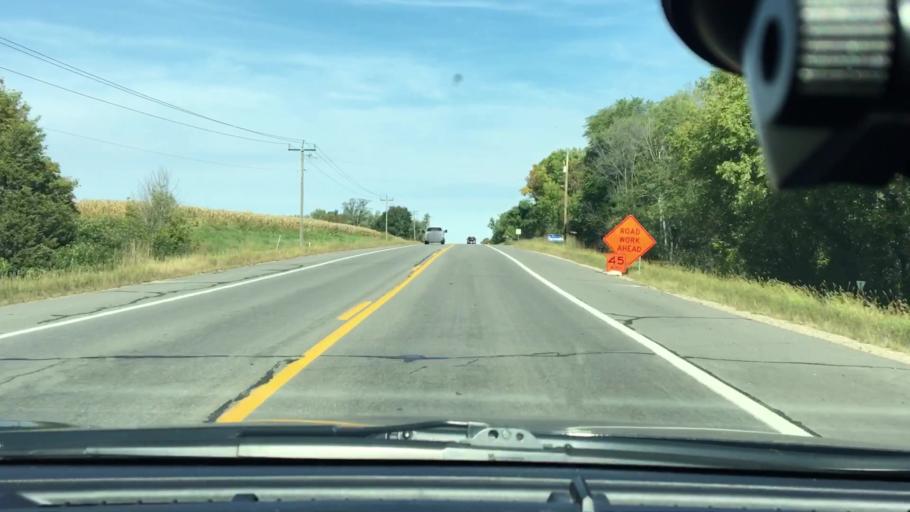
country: US
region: Minnesota
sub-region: Wright County
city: Hanover
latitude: 45.1809
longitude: -93.6655
